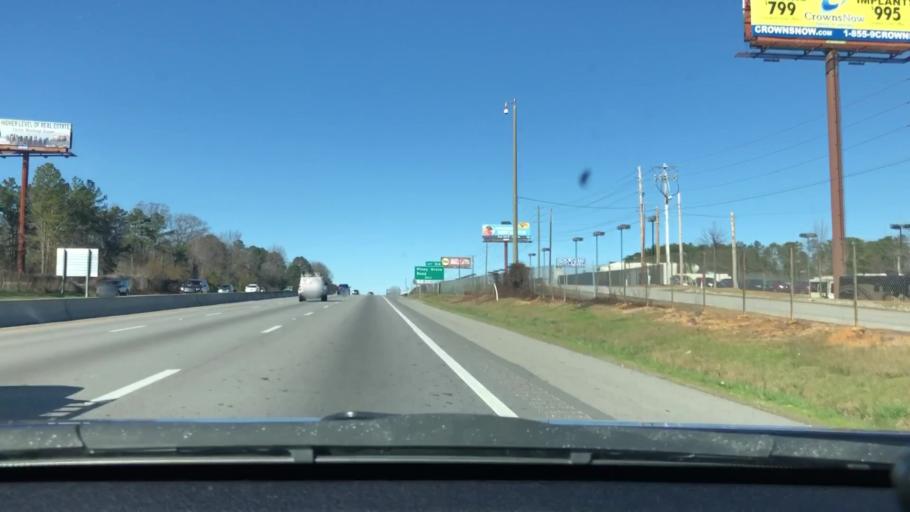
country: US
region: South Carolina
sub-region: Lexington County
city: Saint Andrews
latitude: 34.0533
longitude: -81.1268
